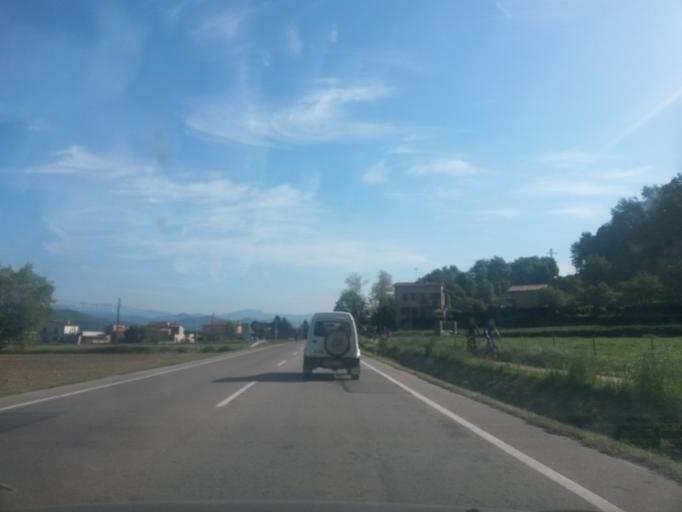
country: ES
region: Catalonia
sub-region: Provincia de Girona
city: Bas
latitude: 42.1372
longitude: 2.4546
